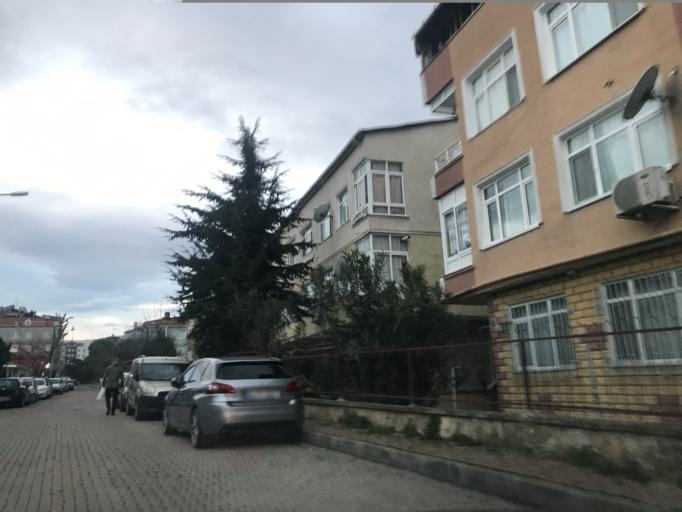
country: TR
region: Istanbul
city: Istanbul
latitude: 41.0427
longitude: 28.9240
